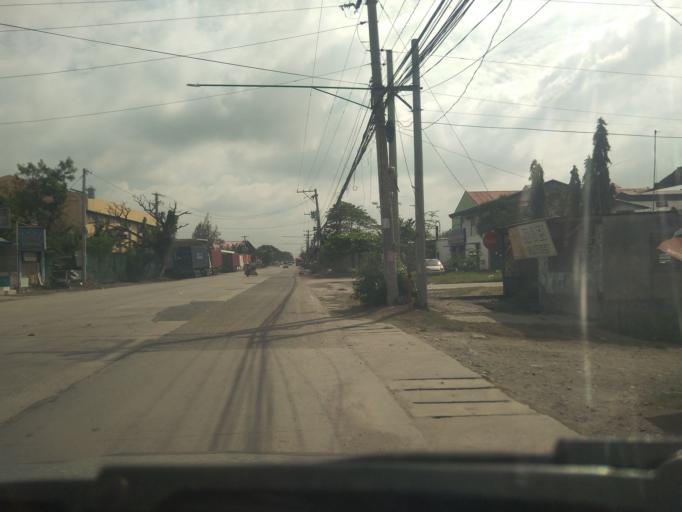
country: PH
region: Central Luzon
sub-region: Province of Pampanga
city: Pau
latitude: 15.0035
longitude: 120.7215
